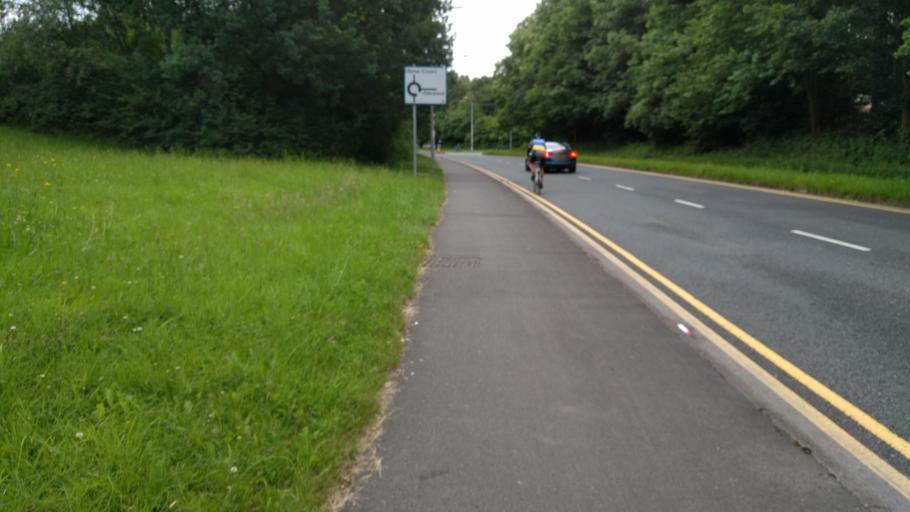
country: GB
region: England
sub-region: Warrington
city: Culcheth
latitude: 53.4224
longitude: -2.5179
